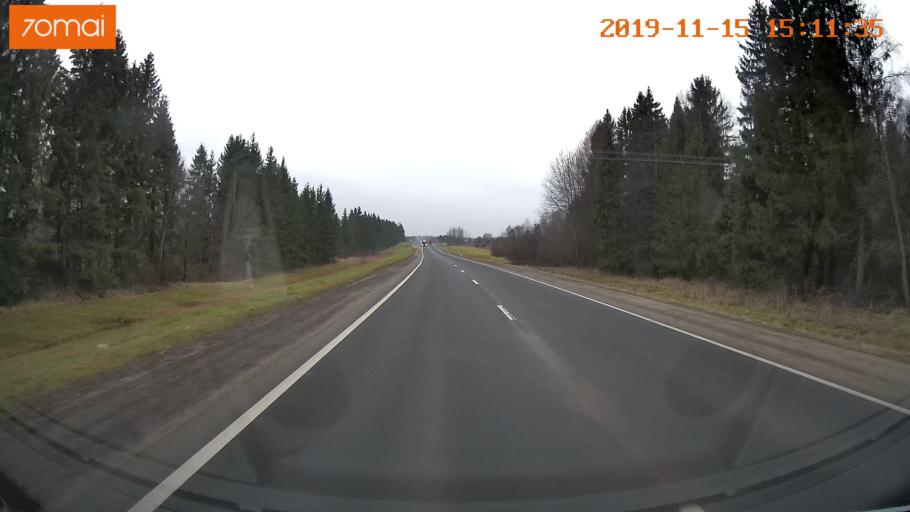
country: RU
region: Jaroslavl
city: Prechistoye
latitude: 58.3349
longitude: 40.2391
